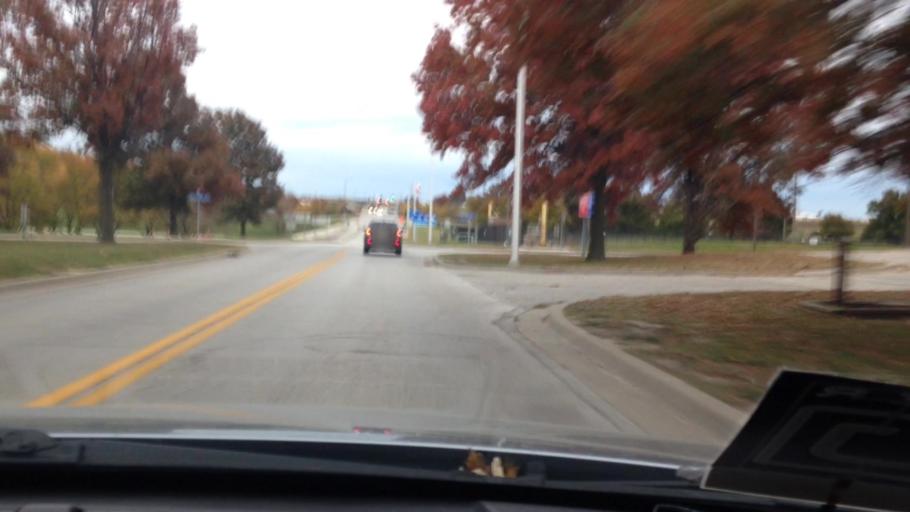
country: US
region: Missouri
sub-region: Platte County
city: Weatherby Lake
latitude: 39.3032
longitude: -94.7180
